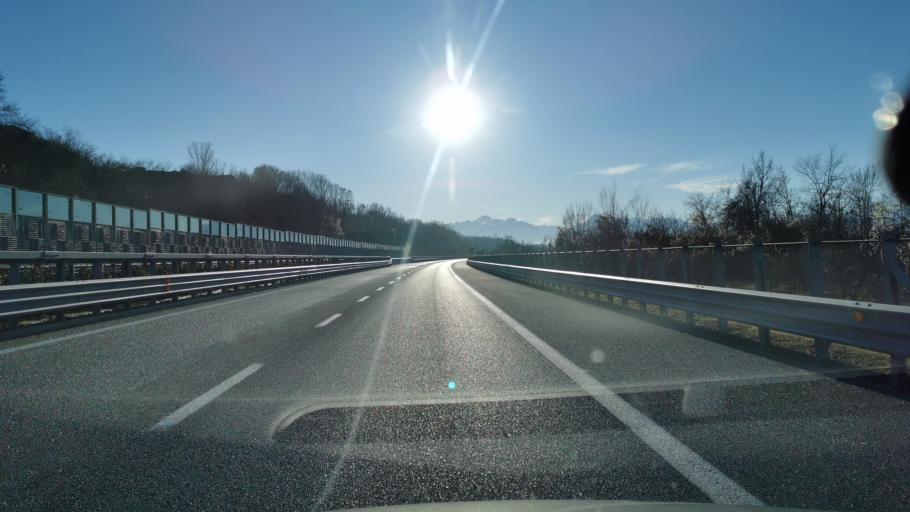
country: IT
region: Piedmont
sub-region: Provincia di Cuneo
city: Montanera
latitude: 44.4625
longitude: 7.6619
